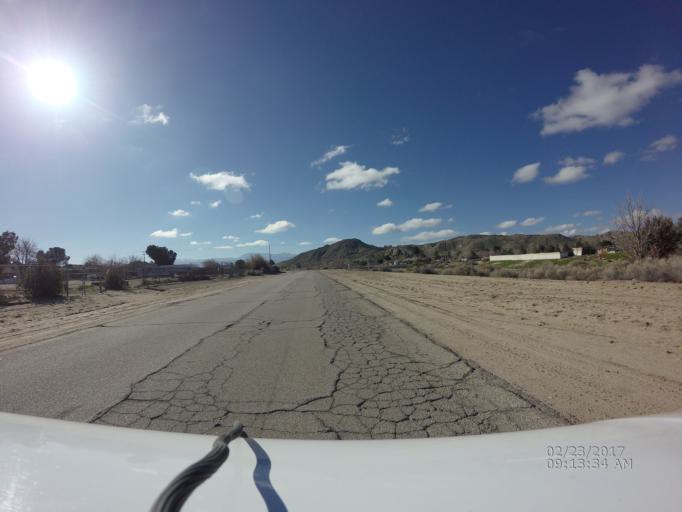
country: US
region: California
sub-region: Los Angeles County
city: Lake Los Angeles
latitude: 34.6175
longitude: -117.8356
